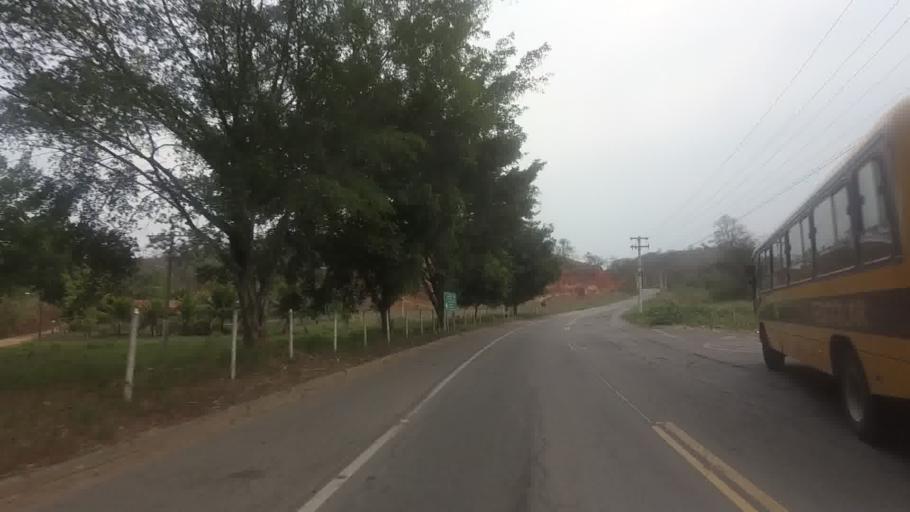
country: BR
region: Rio de Janeiro
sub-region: Santo Antonio De Padua
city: Santo Antonio de Padua
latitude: -21.5644
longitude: -42.1909
